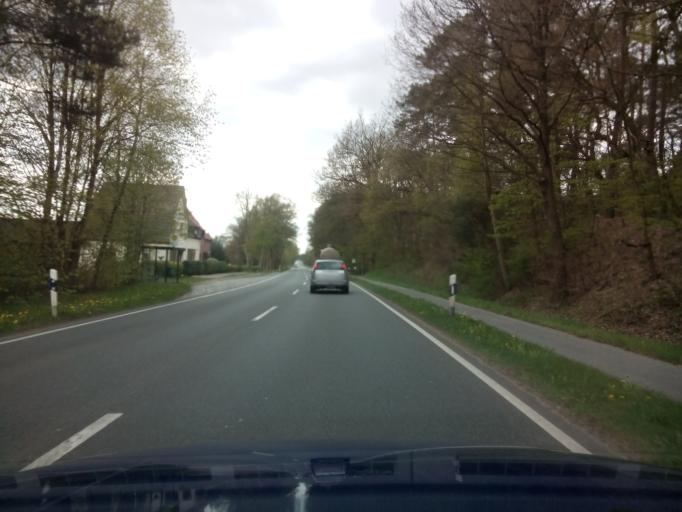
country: DE
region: Lower Saxony
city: Hambergen
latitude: 53.2820
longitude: 8.8237
